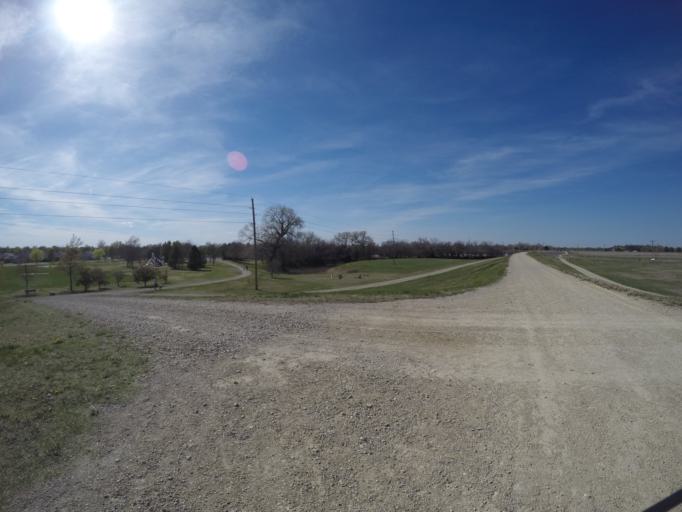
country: US
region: Kansas
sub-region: Saline County
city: Salina
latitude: 38.8233
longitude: -97.5870
